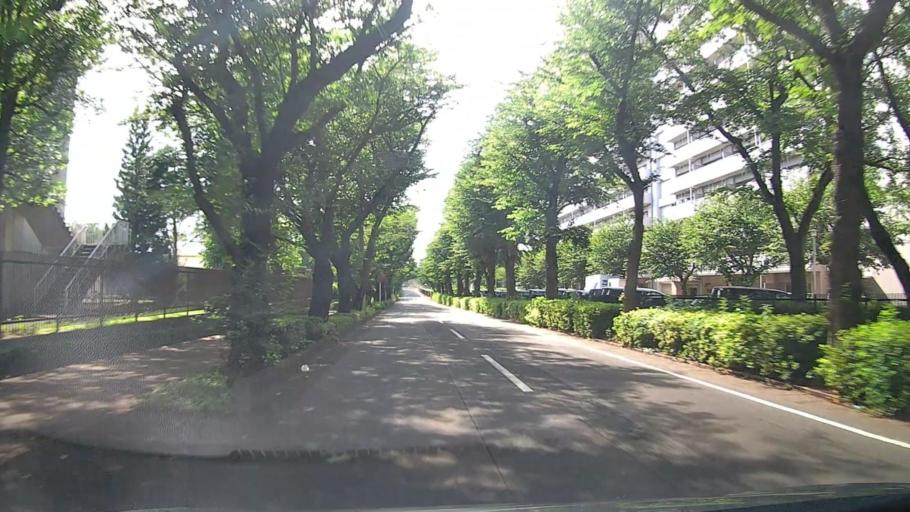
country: JP
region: Saitama
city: Wako
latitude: 35.7794
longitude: 139.6036
